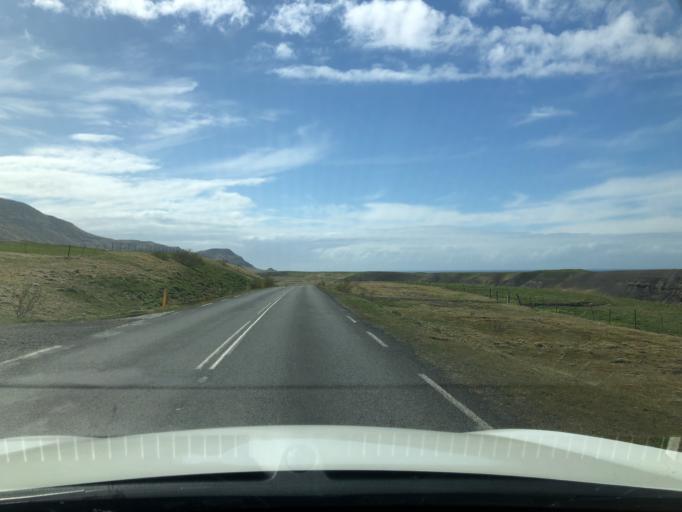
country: IS
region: Capital Region
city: Mosfellsbaer
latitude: 64.3093
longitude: -21.7746
